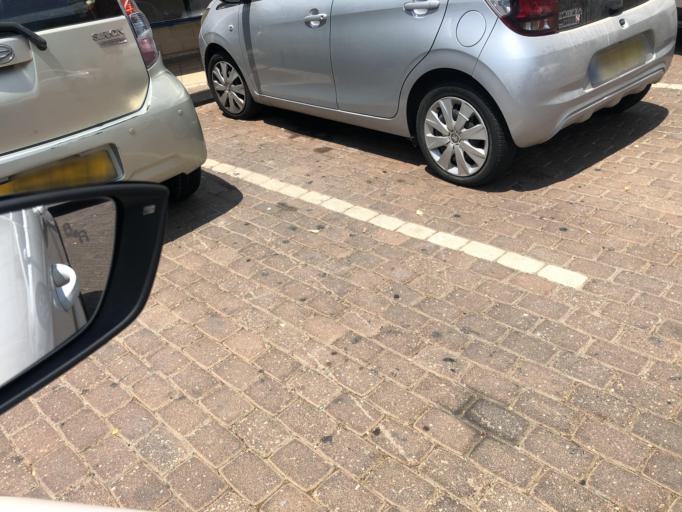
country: IL
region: Haifa
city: Daliyat el Karmil
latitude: 32.6555
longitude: 35.1050
